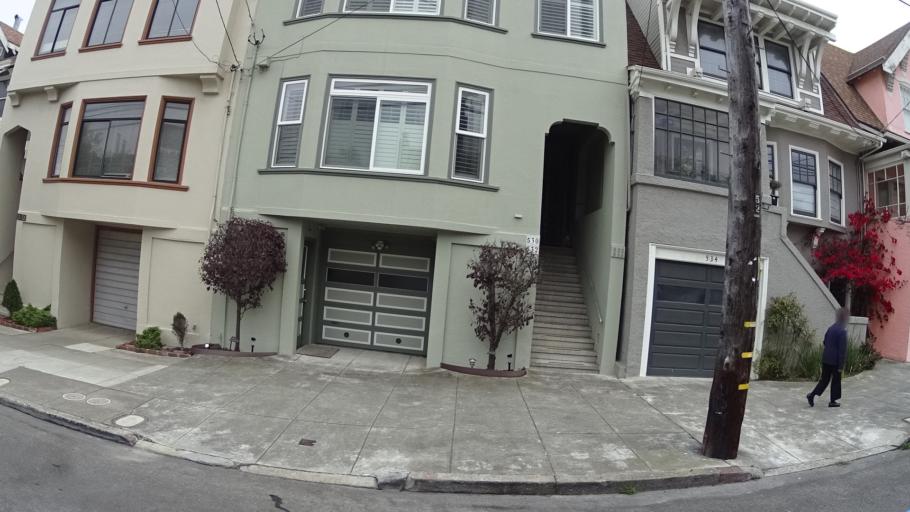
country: US
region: California
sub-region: San Francisco County
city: San Francisco
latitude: 37.7779
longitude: -122.4759
